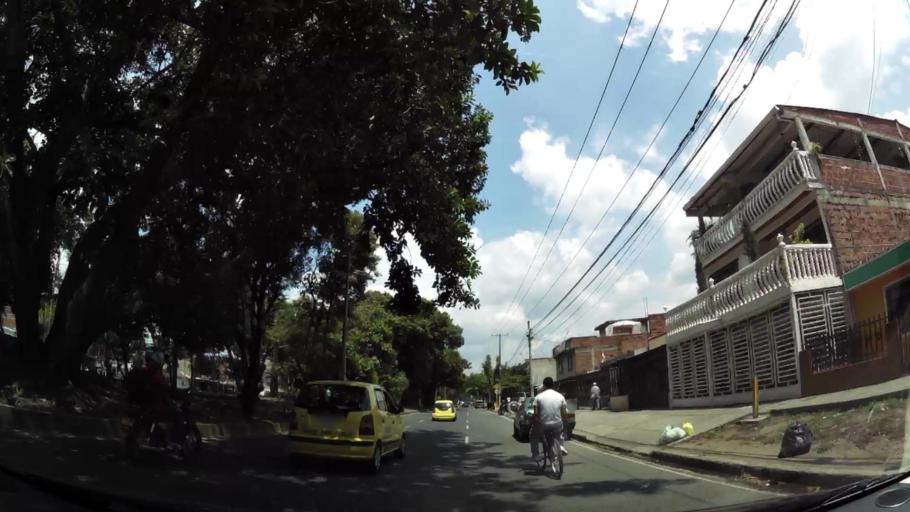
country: CO
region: Valle del Cauca
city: Cali
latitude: 3.4754
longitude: -76.4831
